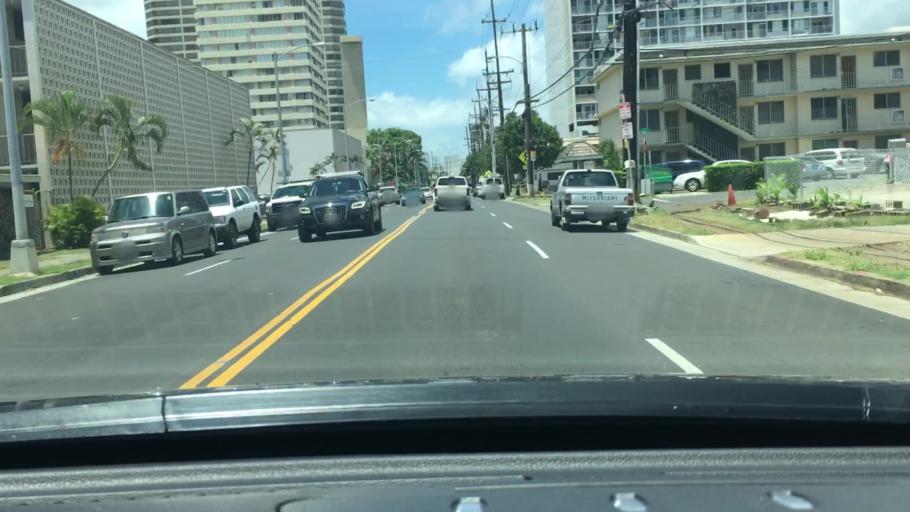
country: US
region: Hawaii
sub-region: Honolulu County
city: Honolulu
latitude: 21.2856
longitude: -157.8215
